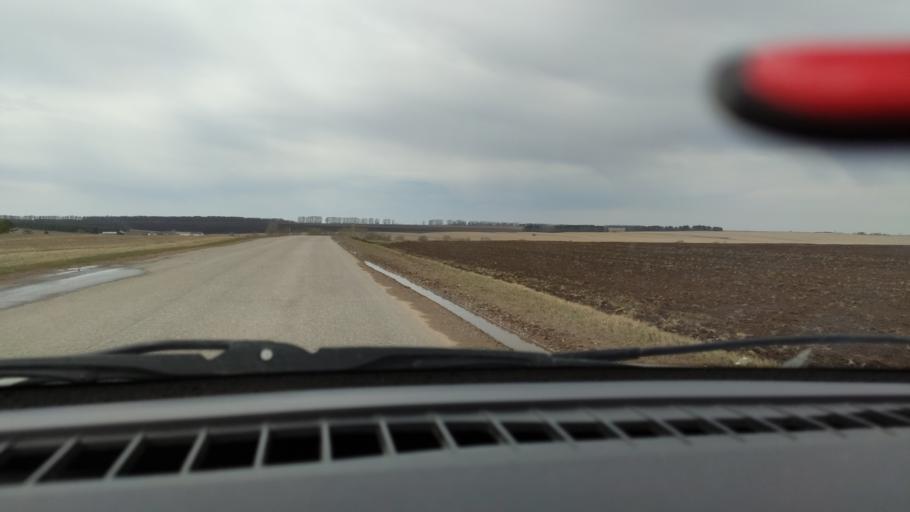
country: RU
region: Bashkortostan
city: Burayevo
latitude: 55.8024
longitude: 55.3525
